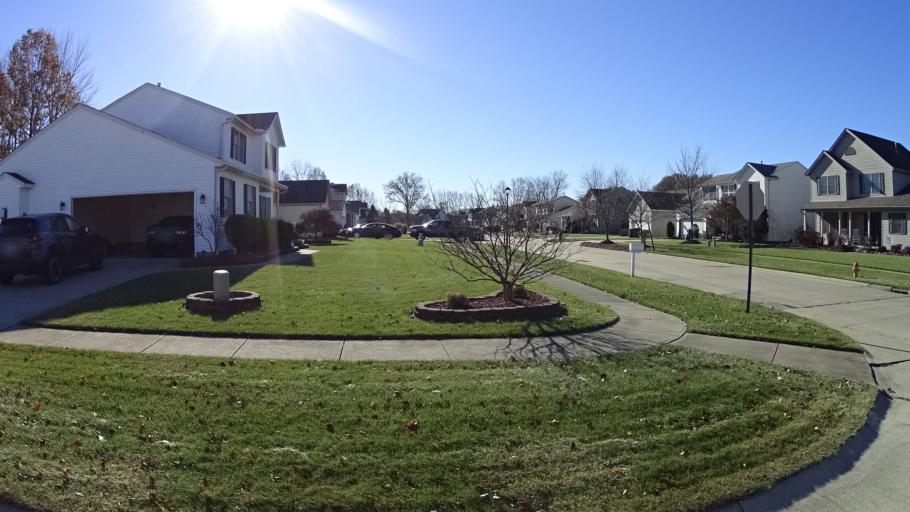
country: US
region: Ohio
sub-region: Lorain County
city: Elyria
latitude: 41.3503
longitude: -82.0727
